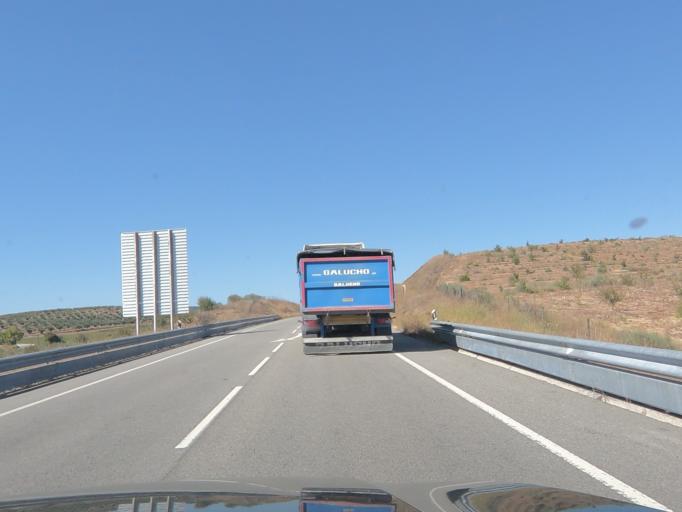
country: PT
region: Vila Real
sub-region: Valpacos
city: Valpacos
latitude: 41.5428
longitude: -7.2559
